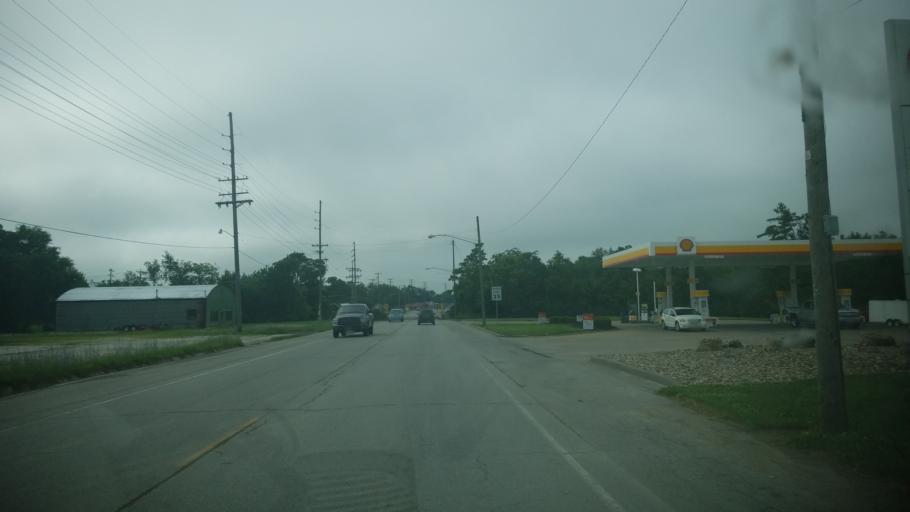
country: US
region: Missouri
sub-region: Pike County
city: Bowling Green
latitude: 39.3473
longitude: -91.2056
